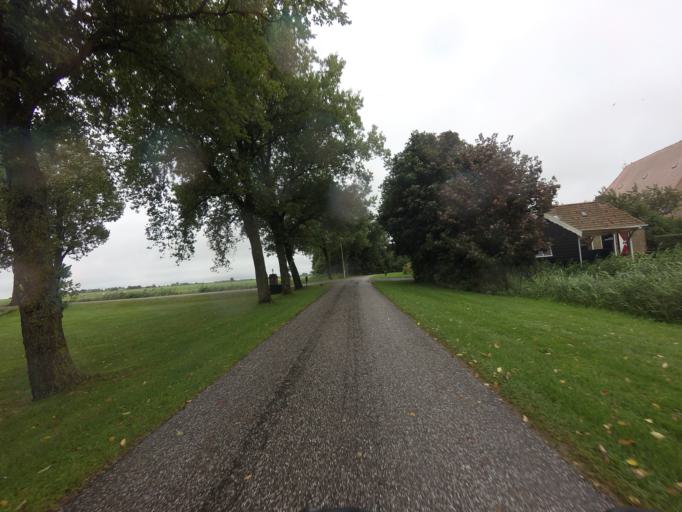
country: NL
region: Friesland
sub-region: Sudwest Fryslan
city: Workum
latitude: 52.9854
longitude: 5.4910
